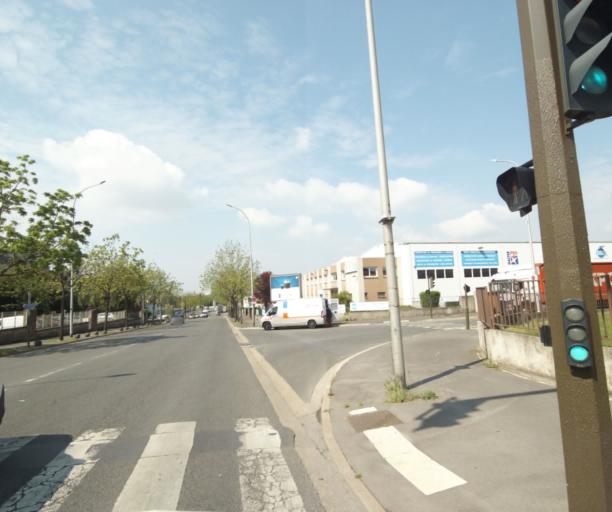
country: FR
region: Ile-de-France
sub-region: Departement des Yvelines
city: Sartrouville
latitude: 48.9512
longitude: 2.2101
